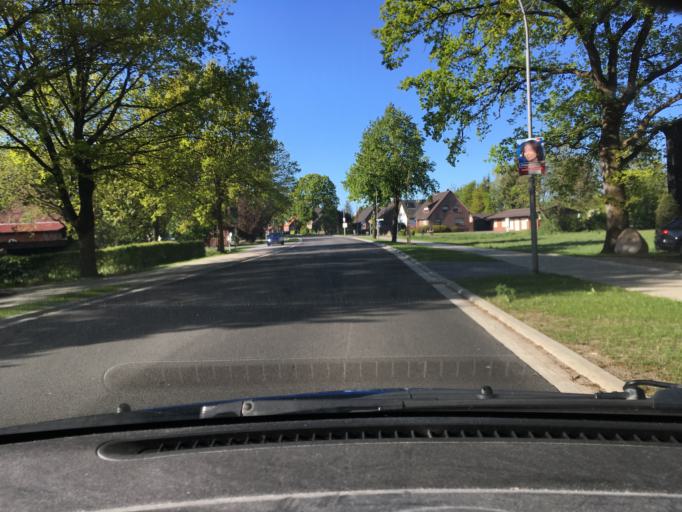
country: DE
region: Lower Saxony
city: Schneverdingen
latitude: 53.0722
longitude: 9.8630
